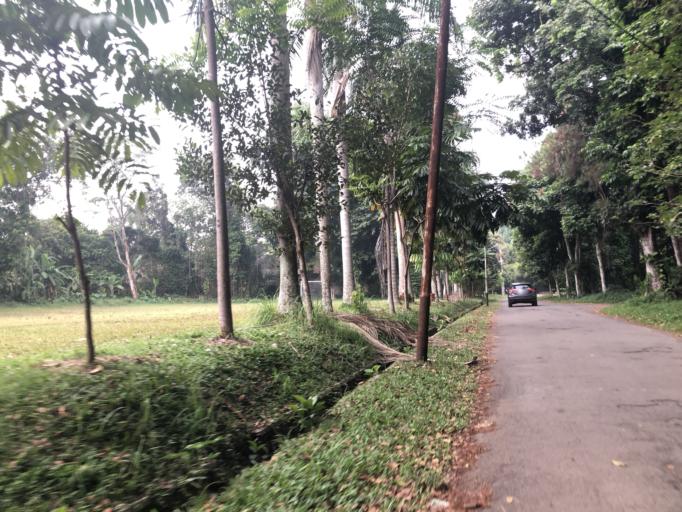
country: ID
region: West Java
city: Ciampea
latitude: -6.5538
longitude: 106.7227
